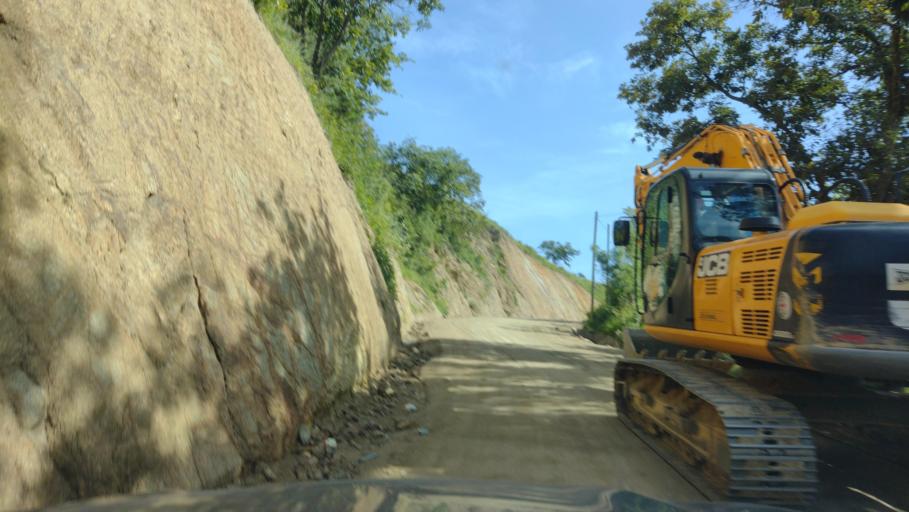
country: GT
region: Guatemala
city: Chinautla
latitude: 14.7541
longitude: -90.5106
